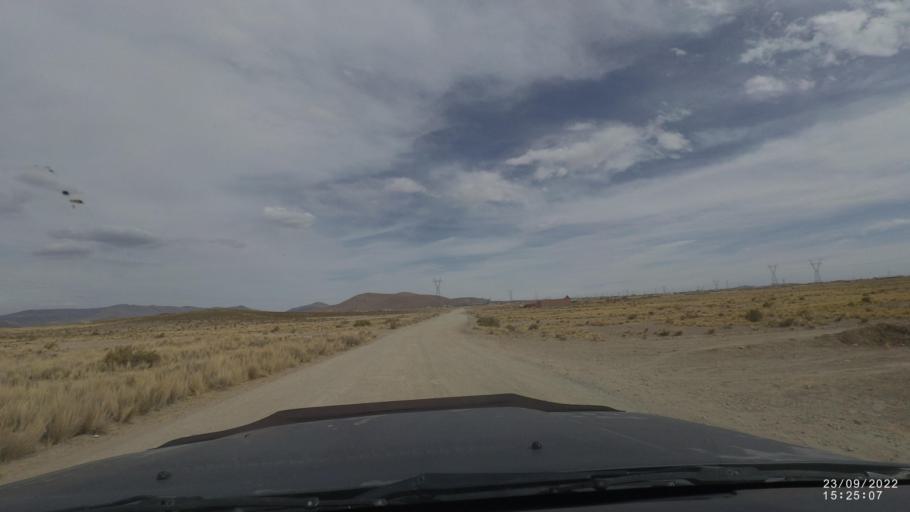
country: BO
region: Oruro
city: Oruro
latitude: -17.9418
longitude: -67.0400
